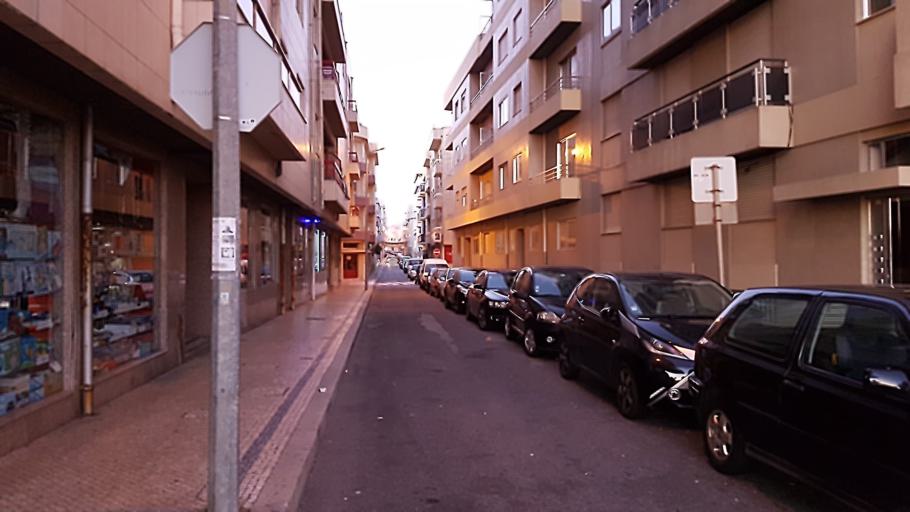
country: PT
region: Porto
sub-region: Povoa de Varzim
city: Povoa de Varzim
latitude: 41.3818
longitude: -8.7698
